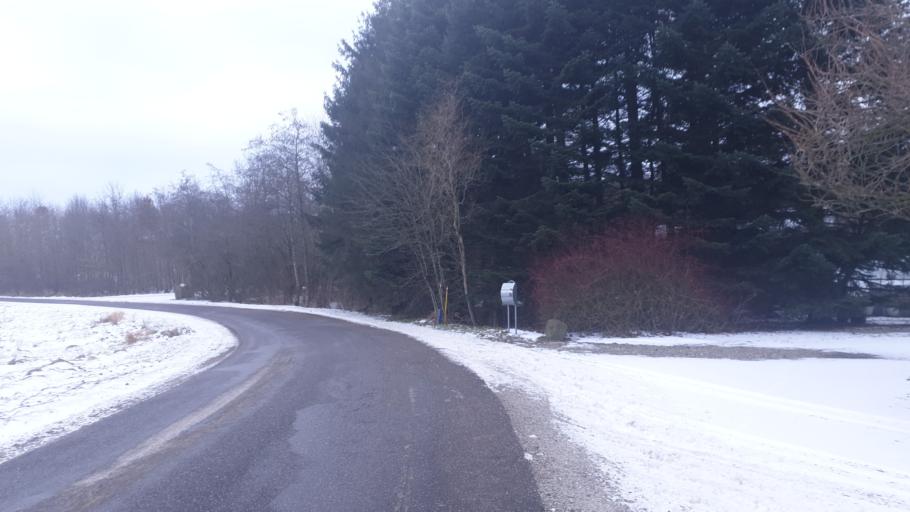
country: DK
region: Central Jutland
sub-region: Hedensted Kommune
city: Hedensted
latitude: 55.7921
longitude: 9.7311
